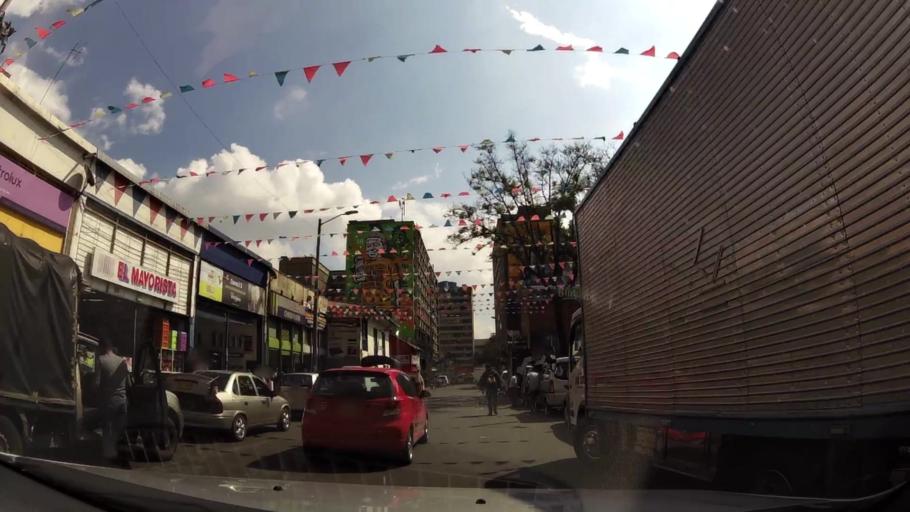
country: CO
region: Bogota D.C.
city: Bogota
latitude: 4.6042
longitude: -74.0782
